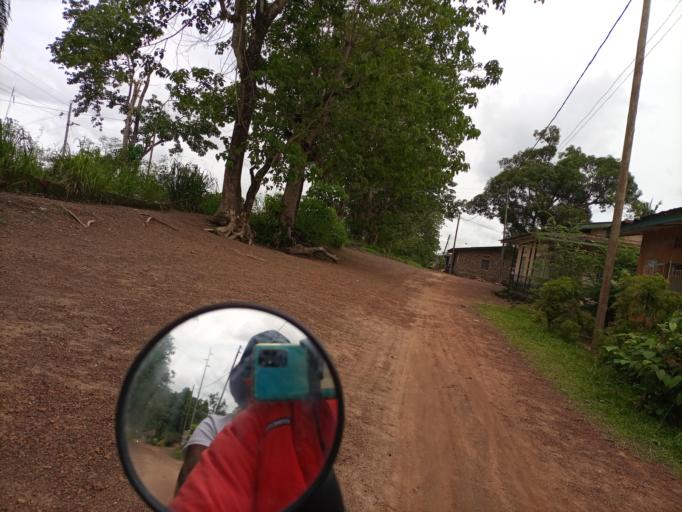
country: SL
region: Southern Province
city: Bo
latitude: 7.9547
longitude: -11.7450
